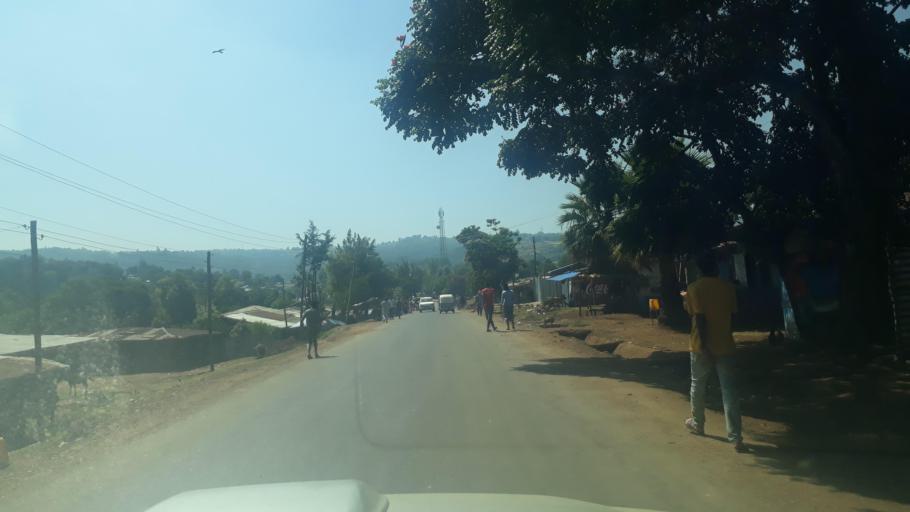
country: ET
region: Oromiya
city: Agaro
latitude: 7.7866
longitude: 36.7275
